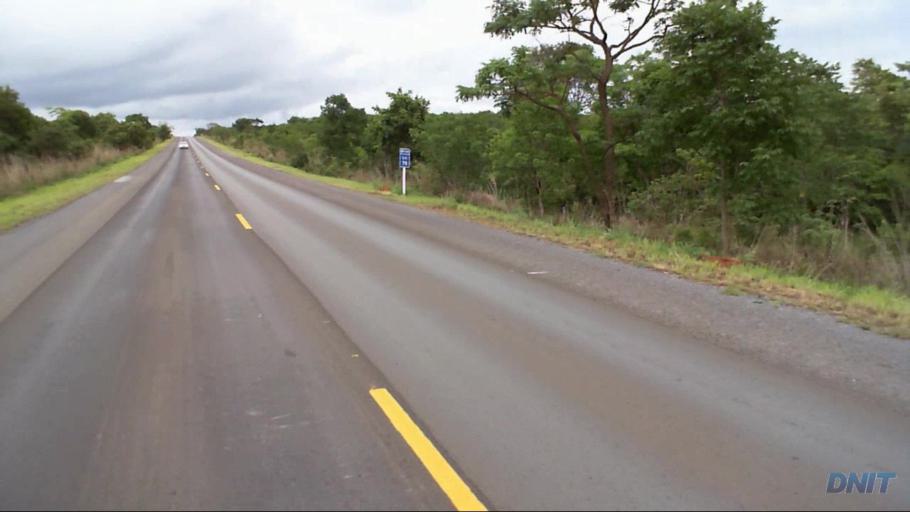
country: BR
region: Goias
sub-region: Padre Bernardo
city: Padre Bernardo
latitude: -15.2168
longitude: -48.5547
